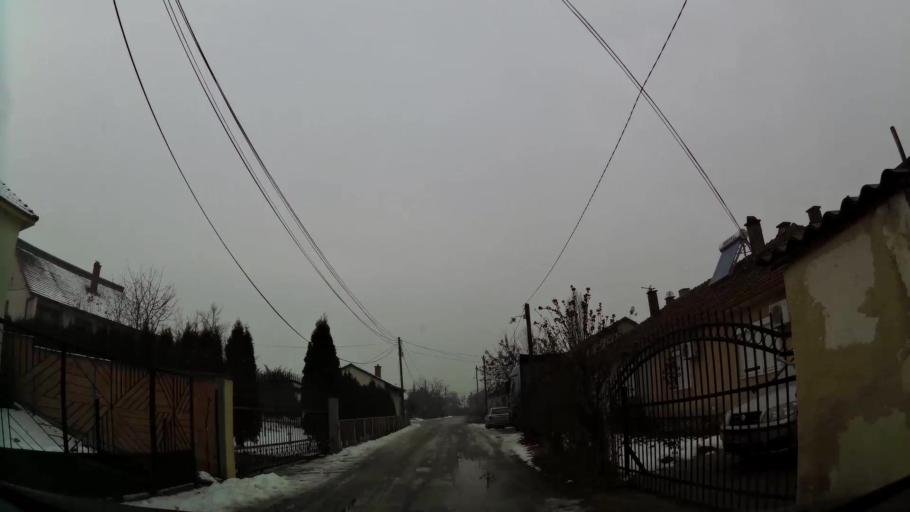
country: MK
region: Petrovec
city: Petrovec
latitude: 41.9382
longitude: 21.6147
